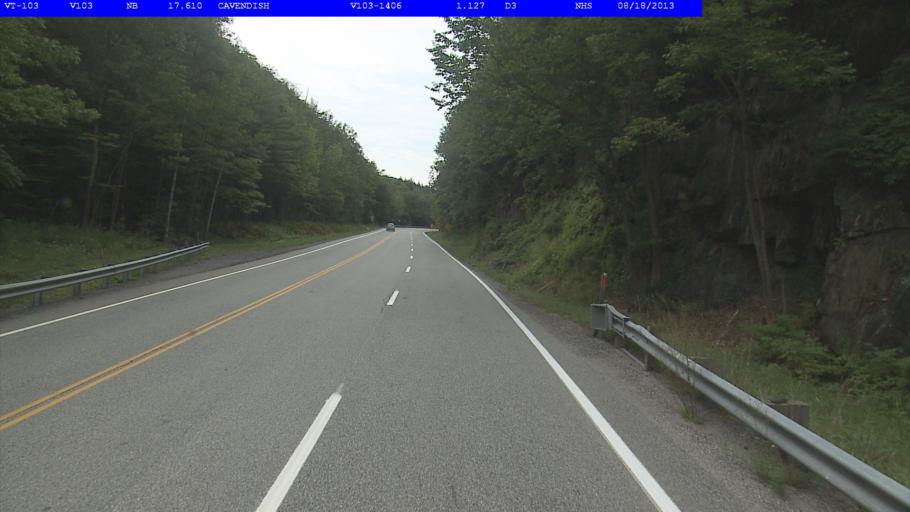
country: US
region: Vermont
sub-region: Windsor County
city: Chester
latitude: 43.3633
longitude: -72.6344
